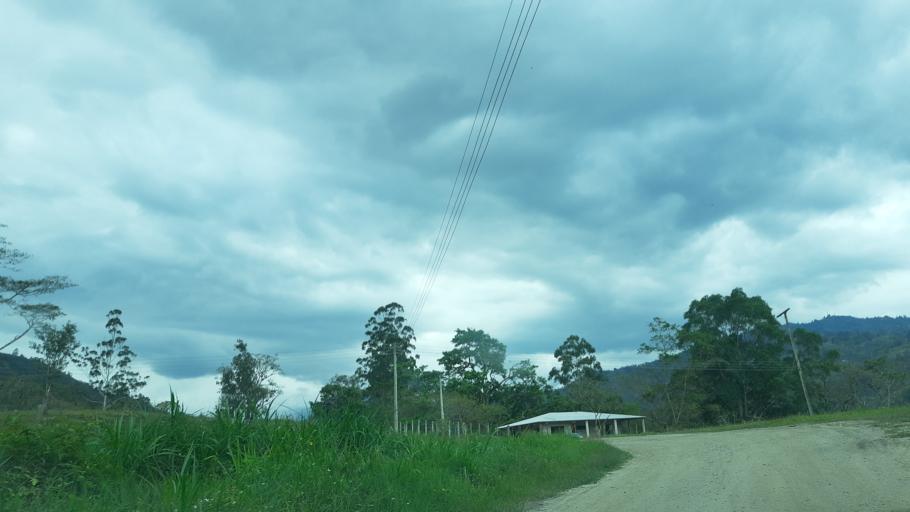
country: CO
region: Boyaca
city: Garagoa
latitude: 5.0677
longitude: -73.3842
